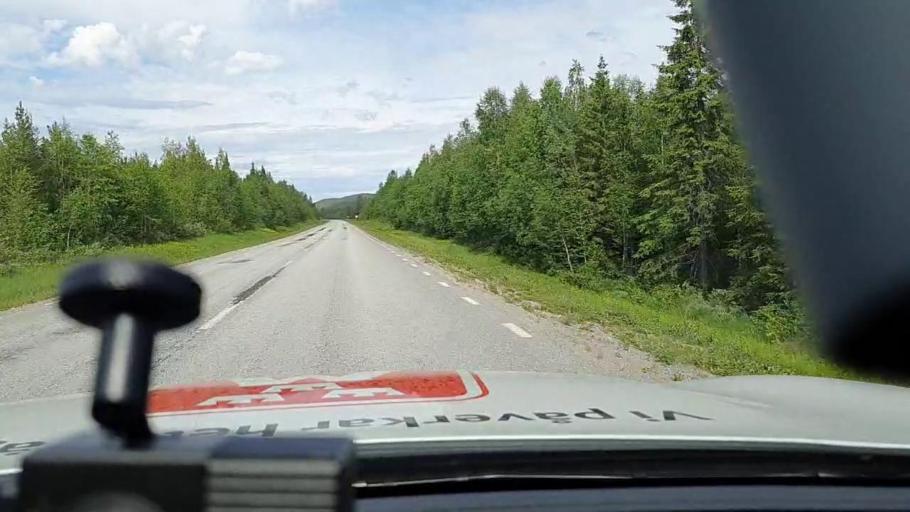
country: SE
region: Norrbotten
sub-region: Jokkmokks Kommun
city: Jokkmokk
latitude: 66.5495
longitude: 20.1242
